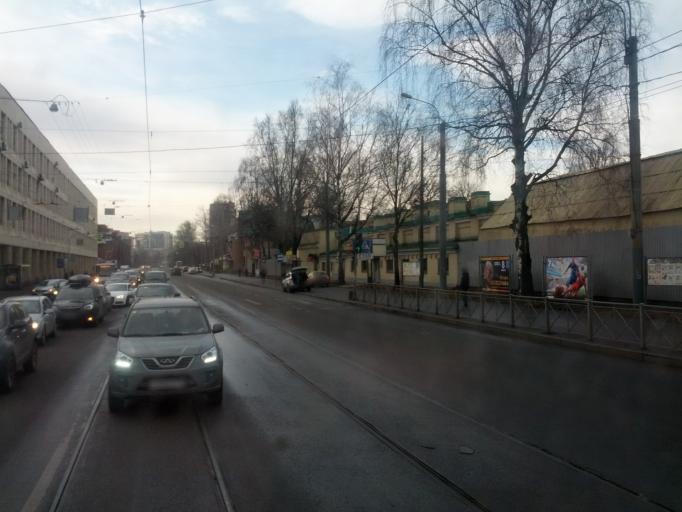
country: RU
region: St.-Petersburg
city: Centralniy
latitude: 59.9419
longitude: 30.4087
